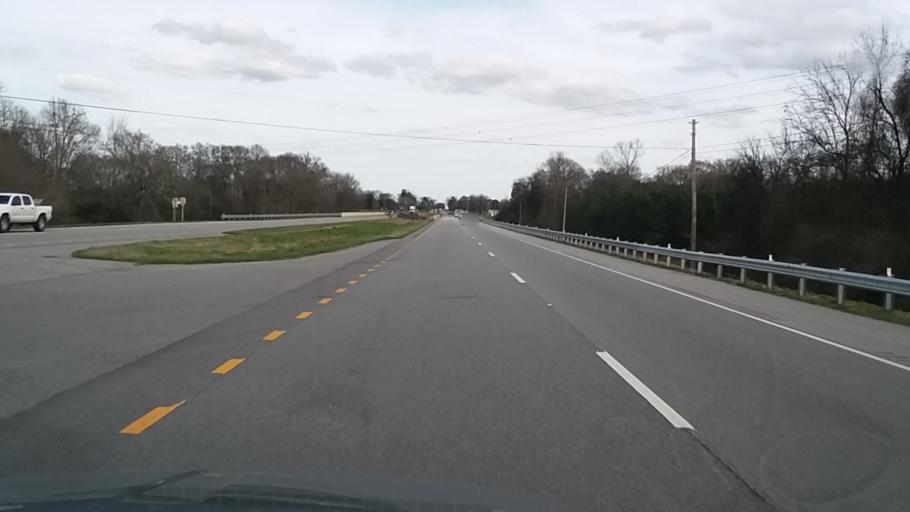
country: US
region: Alabama
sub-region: Lawrence County
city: Town Creek
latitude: 34.6823
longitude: -87.4541
